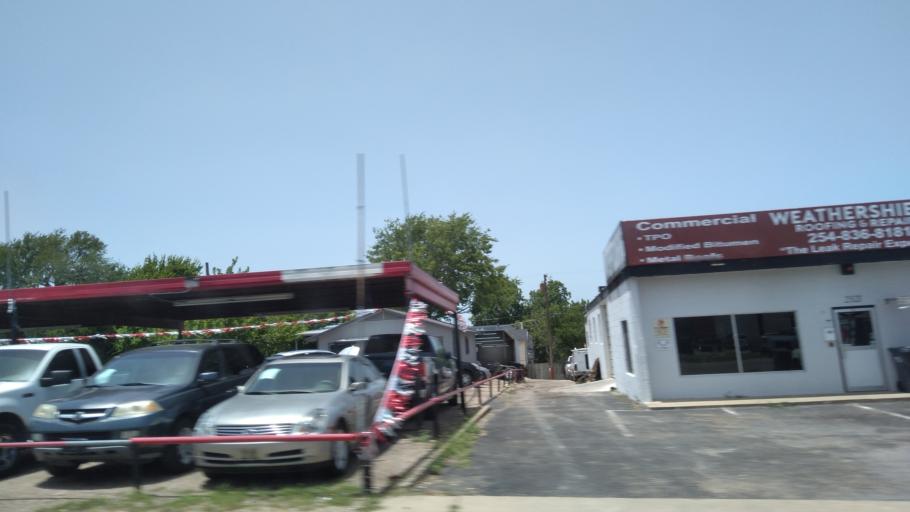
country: US
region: Texas
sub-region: McLennan County
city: Waco
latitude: 31.5408
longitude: -97.1482
